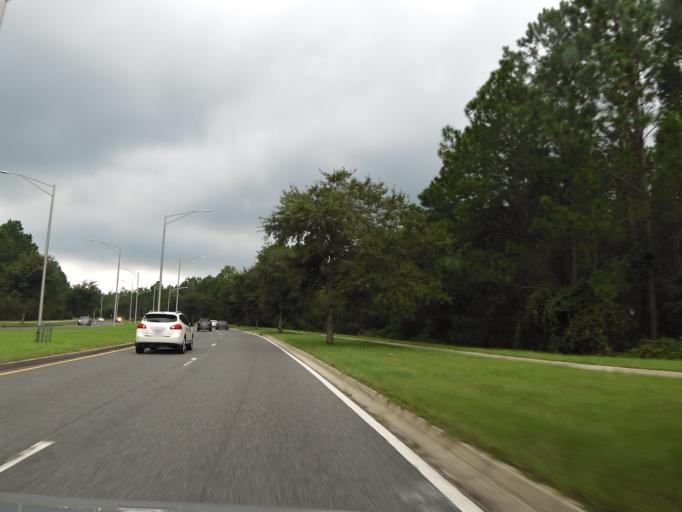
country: US
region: Florida
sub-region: Clay County
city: Lakeside
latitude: 30.1950
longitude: -81.8451
